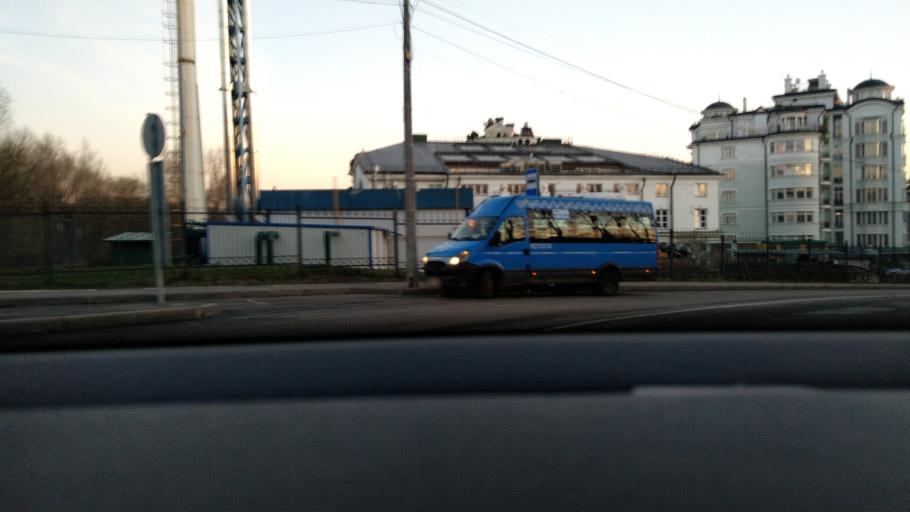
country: RU
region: Moskovskaya
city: Levoberezhnyy
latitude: 55.8308
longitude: 37.4707
